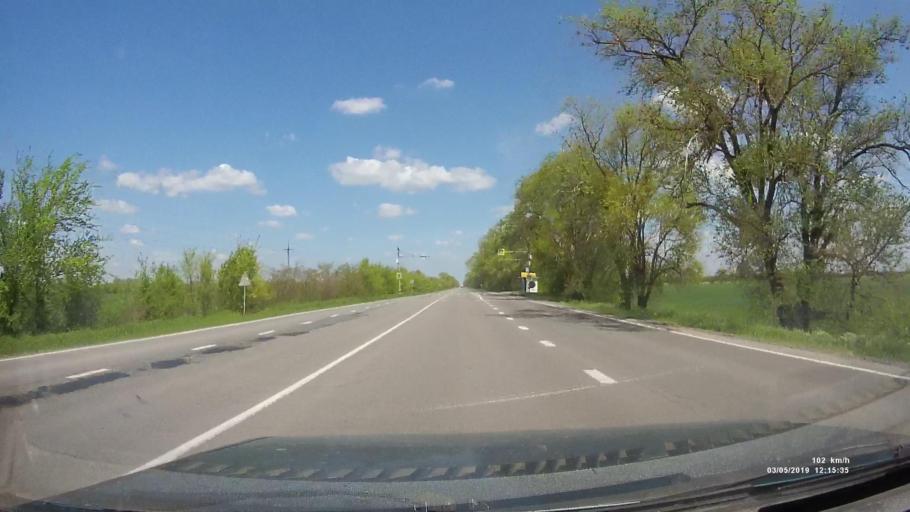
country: RU
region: Rostov
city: Melikhovskaya
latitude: 47.3600
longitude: 40.5754
